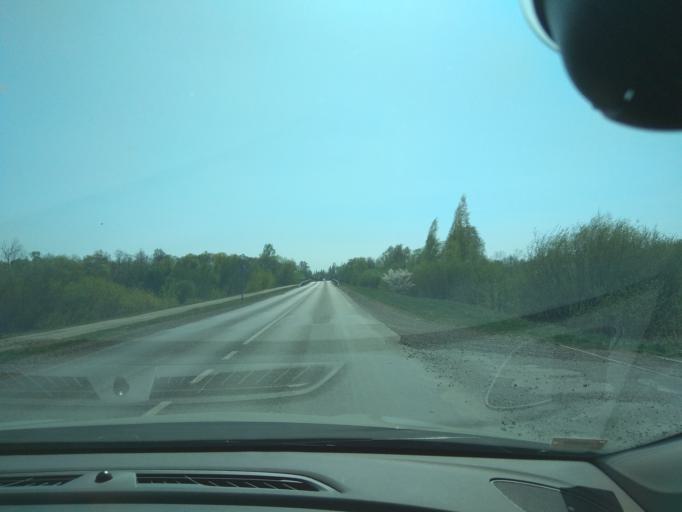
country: LT
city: Linkuva
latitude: 56.0293
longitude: 23.9478
